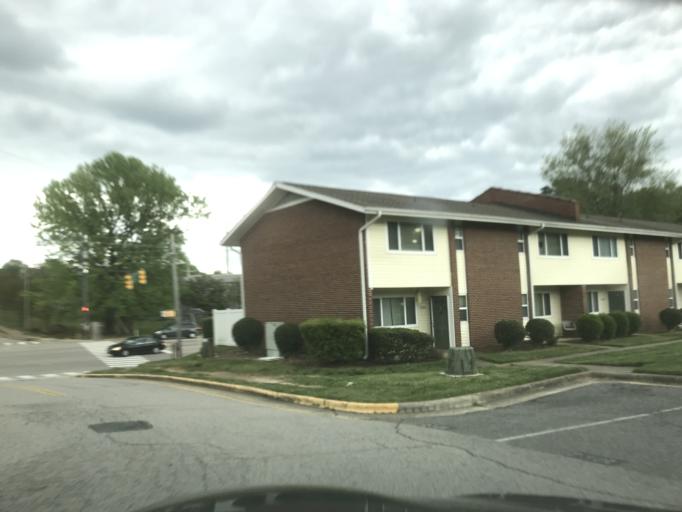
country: US
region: North Carolina
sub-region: Wake County
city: West Raleigh
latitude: 35.7774
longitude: -78.6789
